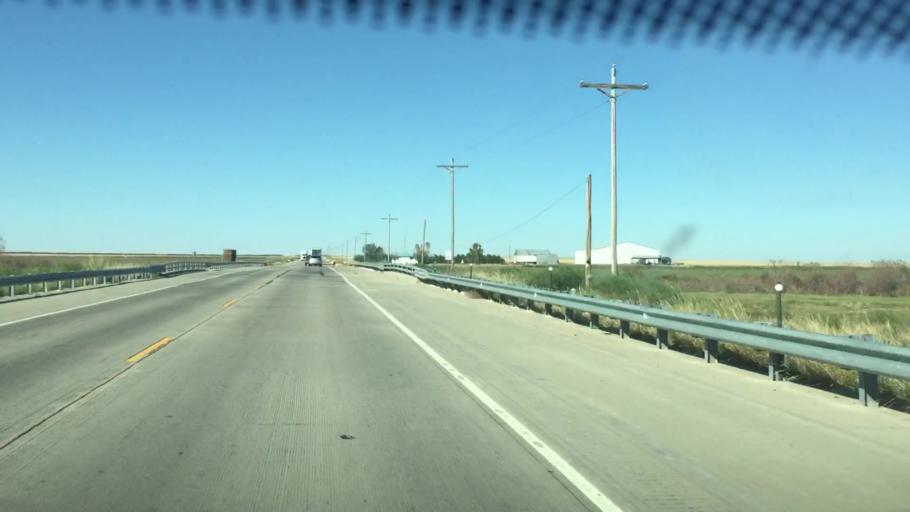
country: US
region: Colorado
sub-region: Prowers County
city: Lamar
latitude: 38.2286
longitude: -102.7240
